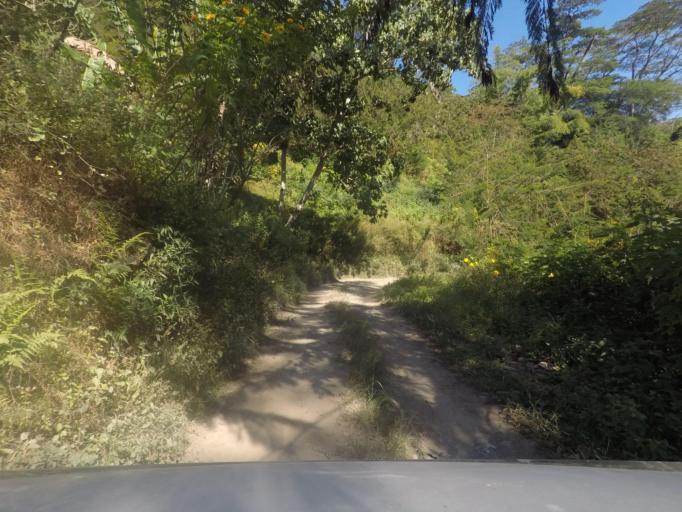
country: TL
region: Ermera
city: Gleno
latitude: -8.7292
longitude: 125.3362
